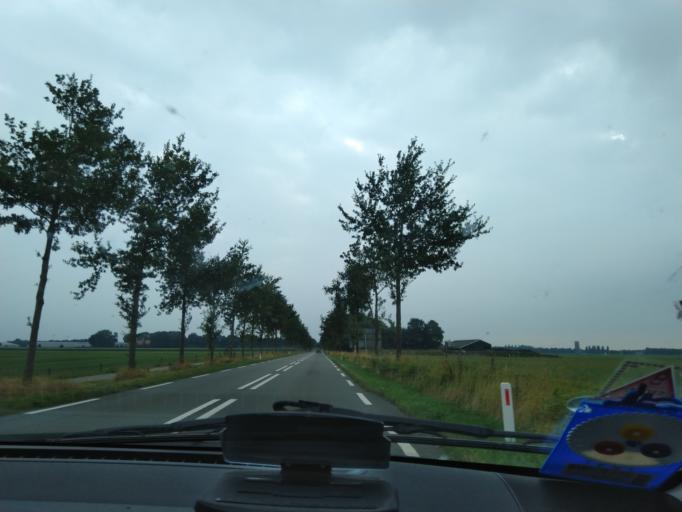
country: NL
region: Groningen
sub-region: Gemeente  Oldambt
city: Winschoten
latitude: 53.1153
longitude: 7.0534
